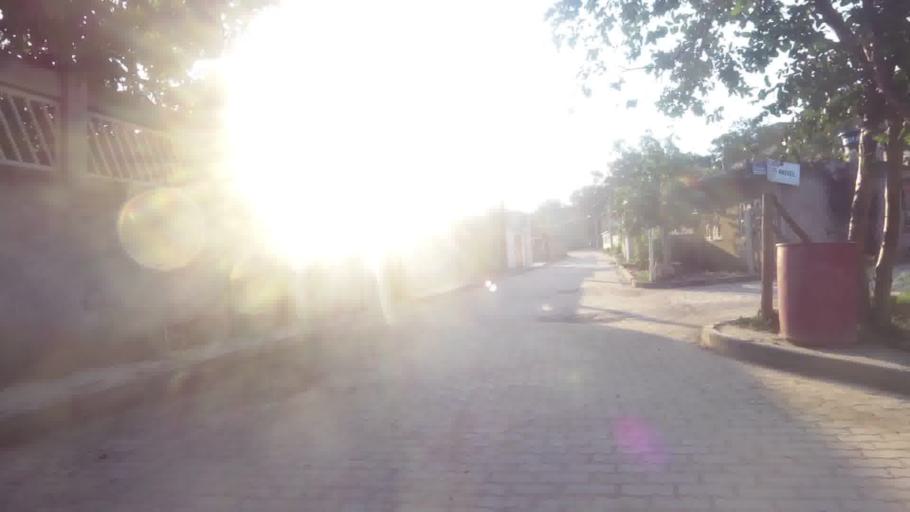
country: BR
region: Espirito Santo
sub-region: Piuma
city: Piuma
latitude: -20.8325
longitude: -40.7235
